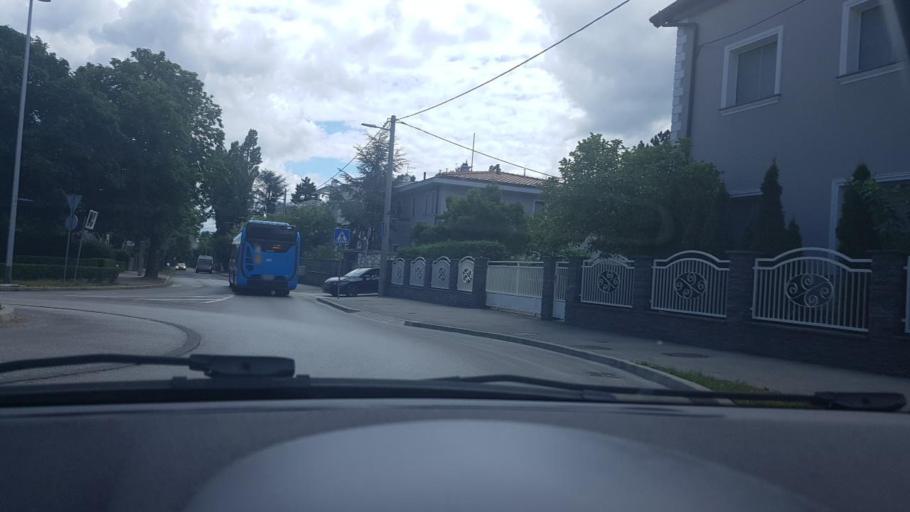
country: HR
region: Grad Zagreb
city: Zagreb
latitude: 45.8271
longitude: 15.9970
